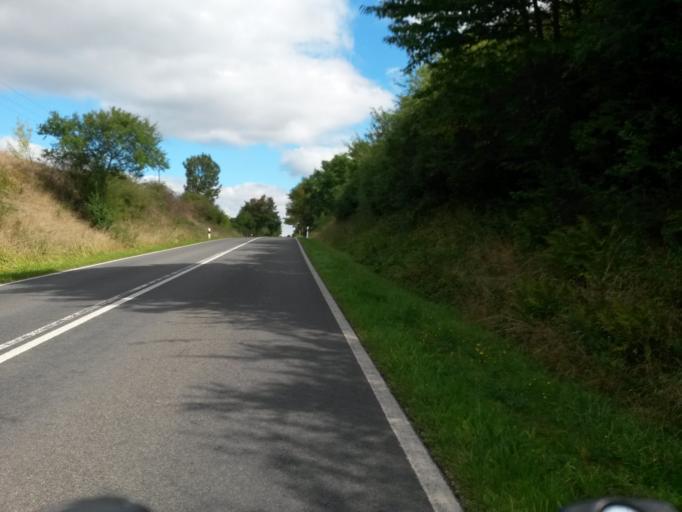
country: DE
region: Brandenburg
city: Mittenwalde
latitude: 53.2122
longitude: 13.5659
